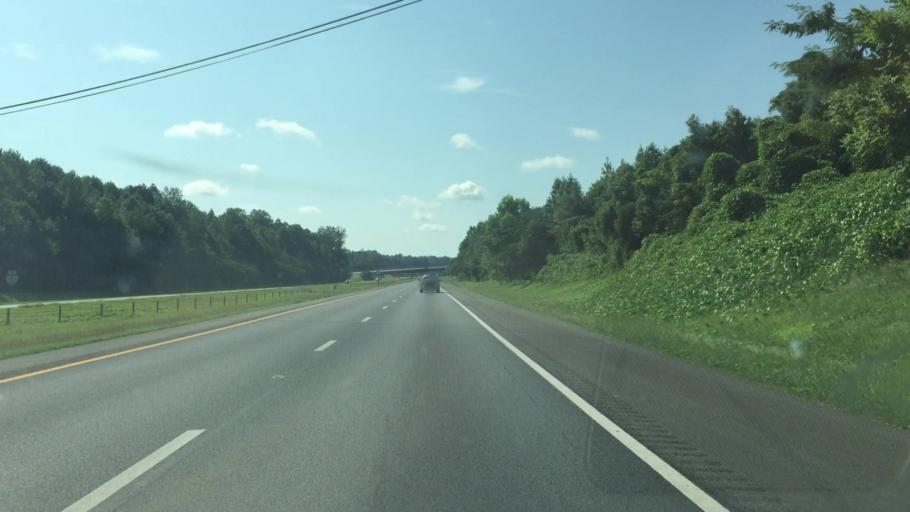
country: US
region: North Carolina
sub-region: Mecklenburg County
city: Mint Hill
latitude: 35.2084
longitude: -80.6400
